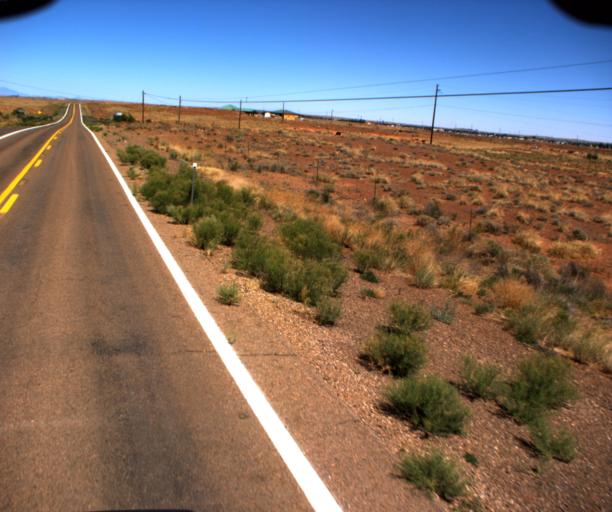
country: US
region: Arizona
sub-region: Navajo County
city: Winslow
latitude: 34.9977
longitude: -110.6758
